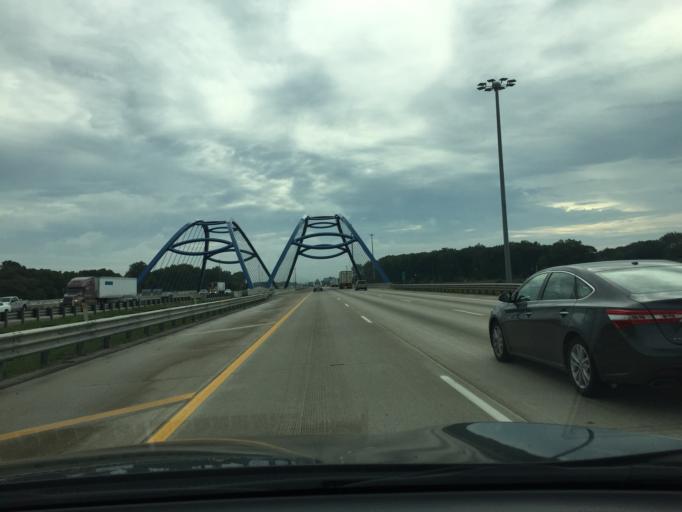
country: US
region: Michigan
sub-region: Wayne County
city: Taylor
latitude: 42.2646
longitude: -83.2725
